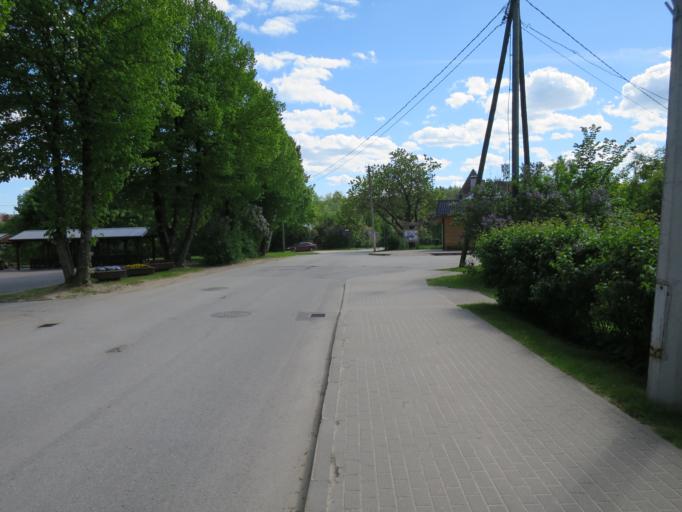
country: LV
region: Baldone
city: Baldone
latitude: 56.7417
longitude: 24.3954
